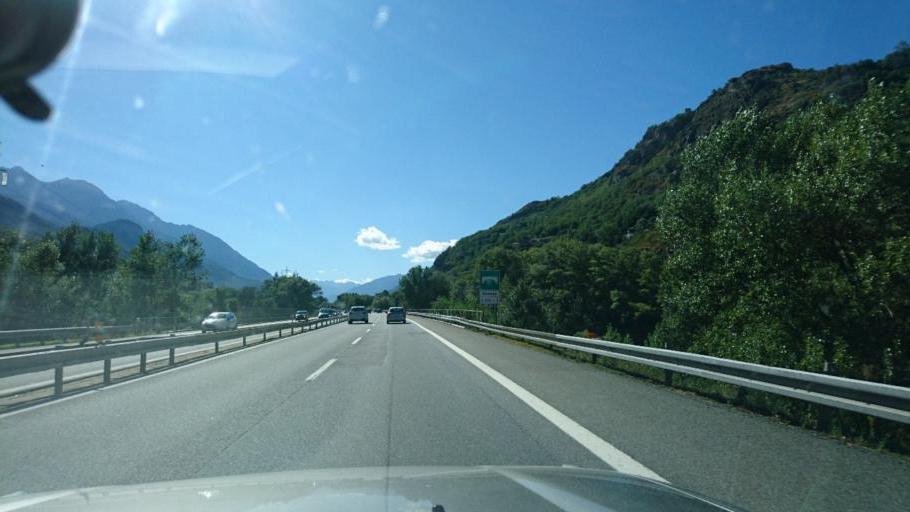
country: IT
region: Aosta Valley
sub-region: Valle d'Aosta
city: Pontey
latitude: 45.7446
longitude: 7.5722
